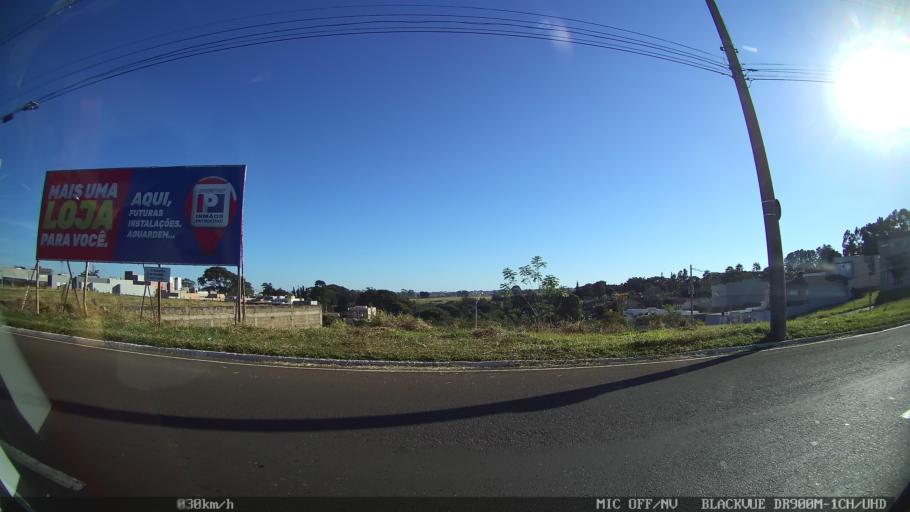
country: BR
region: Sao Paulo
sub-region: Franca
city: Franca
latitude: -20.5635
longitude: -47.3644
